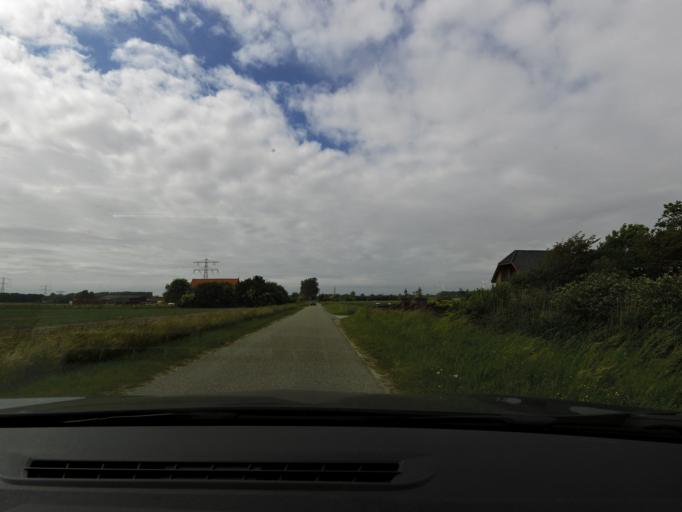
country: NL
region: South Holland
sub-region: Gemeente Brielle
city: Brielle
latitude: 51.9145
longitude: 4.1295
